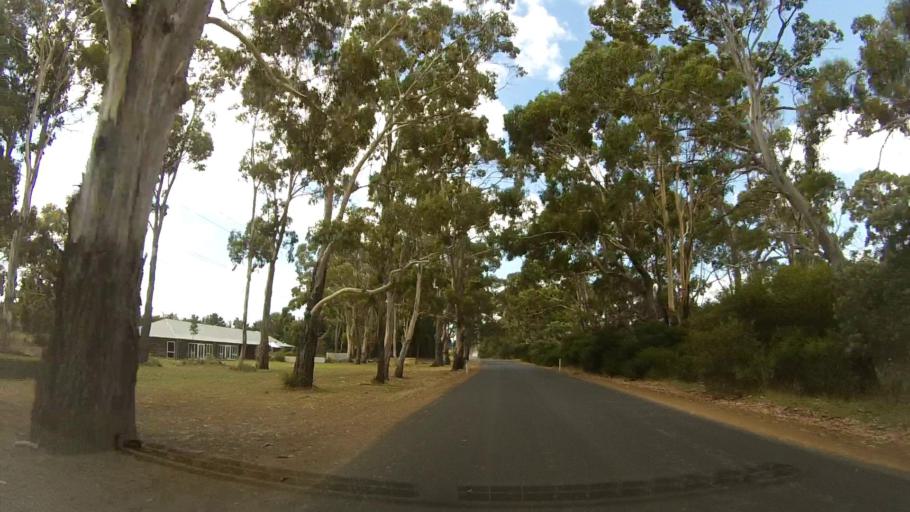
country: AU
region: Tasmania
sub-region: Clarence
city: Seven Mile Beach
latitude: -42.8549
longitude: 147.5128
